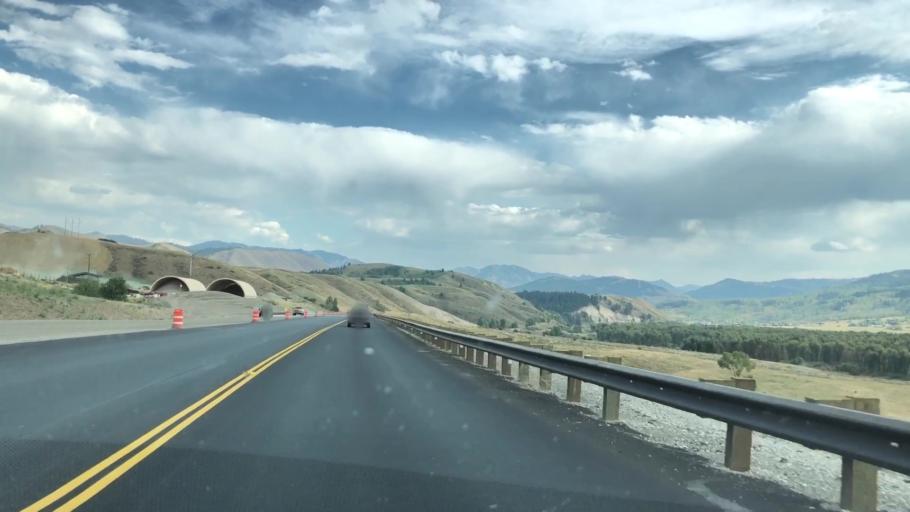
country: US
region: Wyoming
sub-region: Teton County
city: South Park
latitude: 43.4049
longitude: -110.7587
